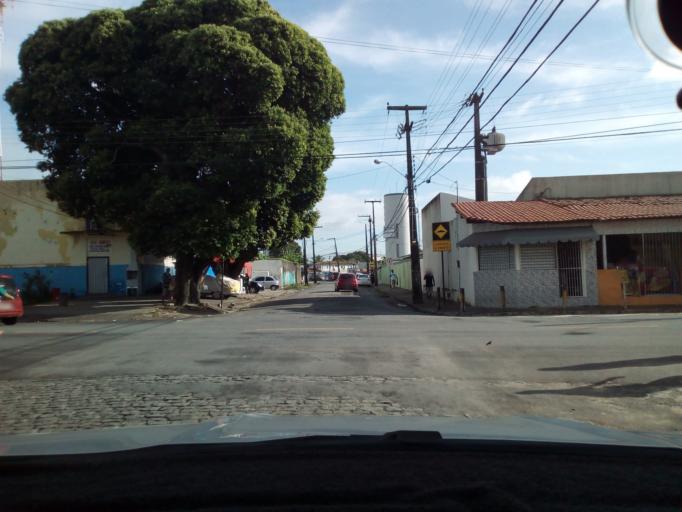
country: BR
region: Paraiba
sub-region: Joao Pessoa
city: Joao Pessoa
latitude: -7.1303
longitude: -34.8755
